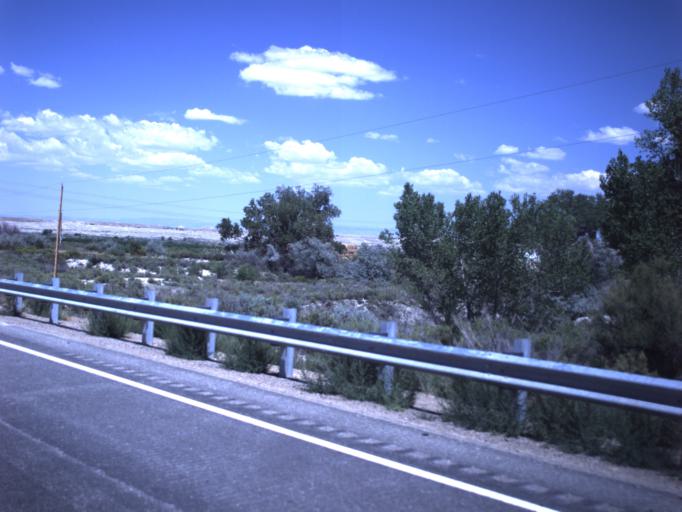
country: US
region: Utah
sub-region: Emery County
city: Huntington
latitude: 39.2961
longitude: -110.9657
